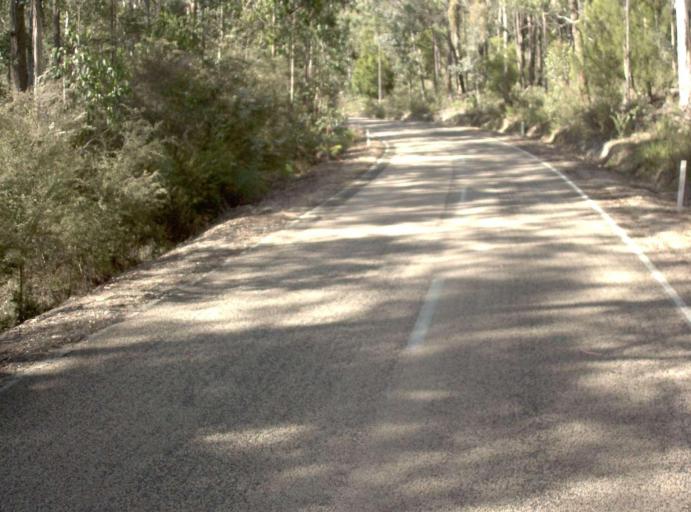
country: AU
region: Victoria
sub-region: East Gippsland
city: Lakes Entrance
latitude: -37.5485
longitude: 148.5551
